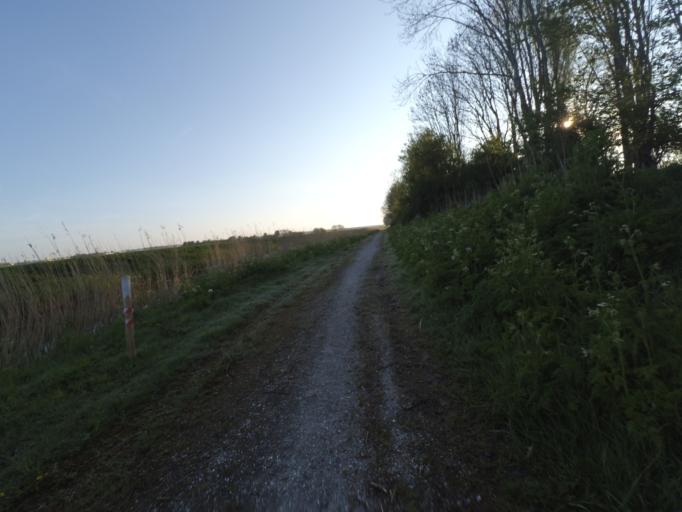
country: NL
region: Flevoland
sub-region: Gemeente Lelystad
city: Lelystad
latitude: 52.4529
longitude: 5.4982
